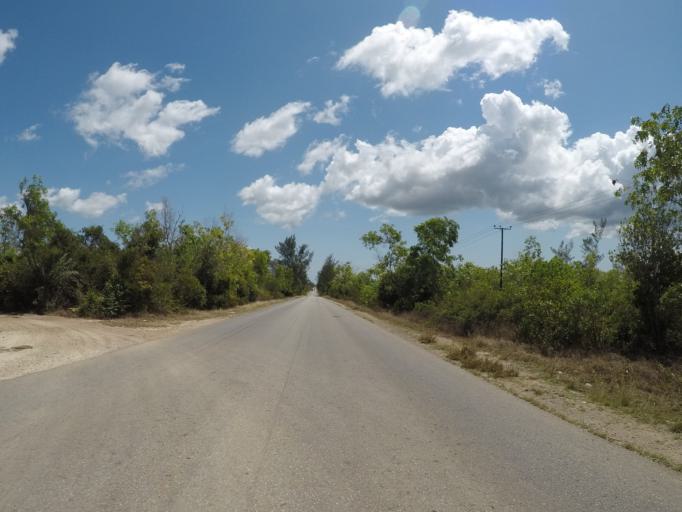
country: TZ
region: Zanzibar Central/South
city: Nganane
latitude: -6.2688
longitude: 39.5171
